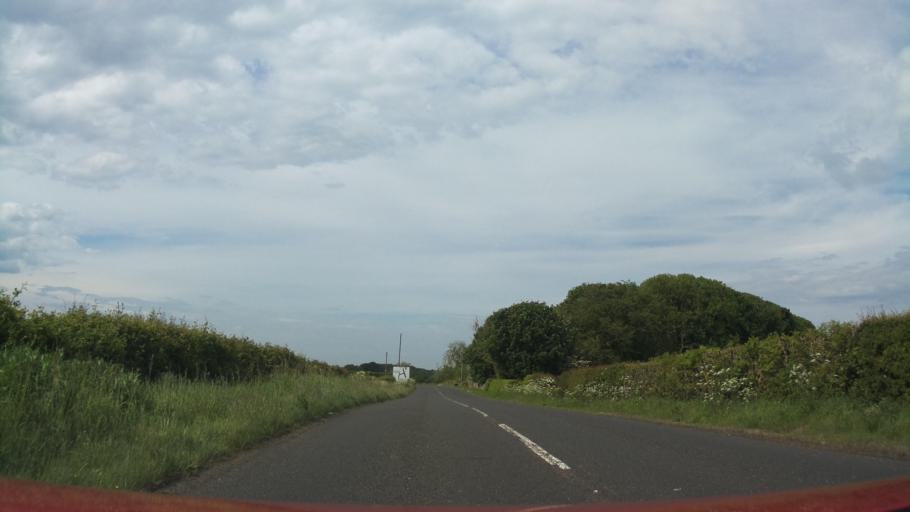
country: GB
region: England
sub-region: Northumberland
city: Ellingham
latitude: 55.4723
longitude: -1.7201
